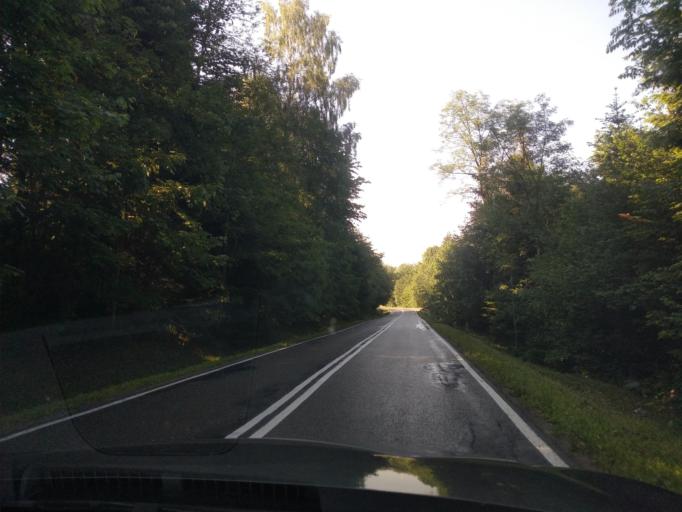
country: PL
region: Subcarpathian Voivodeship
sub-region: Powiat leski
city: Cisna
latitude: 49.2511
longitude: 22.2857
